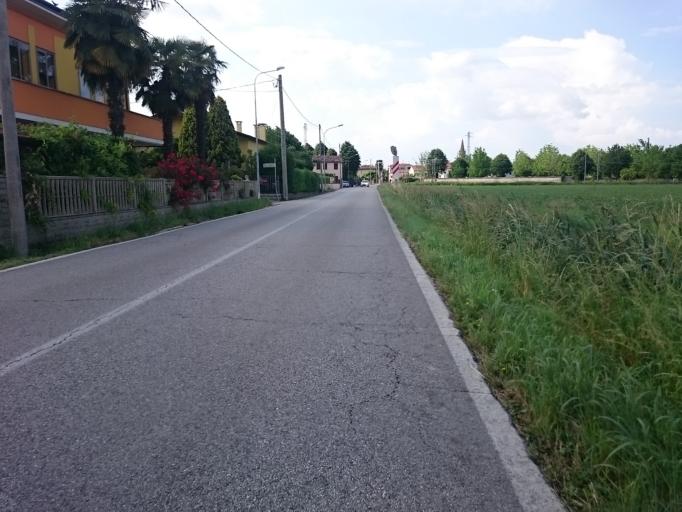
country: IT
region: Veneto
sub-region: Provincia di Padova
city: Montagnana
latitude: 45.2264
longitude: 11.4675
